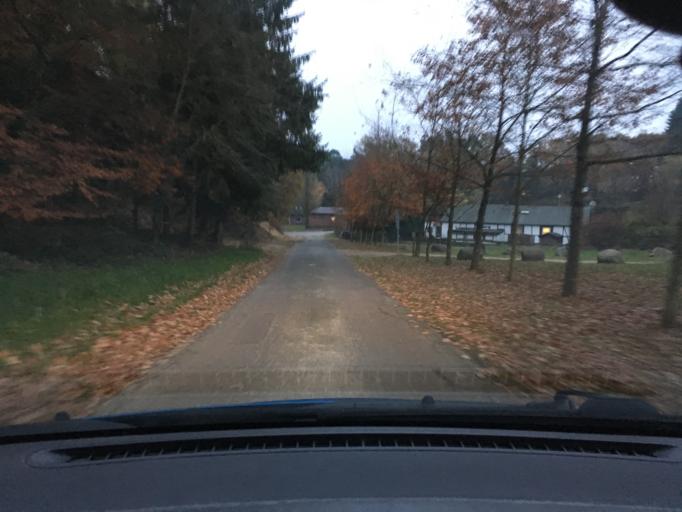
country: DE
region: Lower Saxony
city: Eyendorf
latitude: 53.1756
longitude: 10.1621
